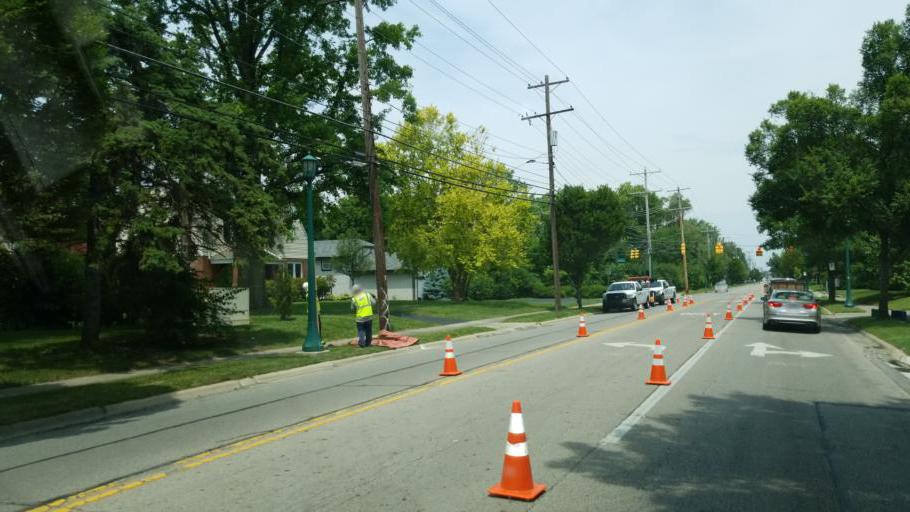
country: US
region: Ohio
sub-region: Franklin County
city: Upper Arlington
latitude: 40.0461
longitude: -83.0668
